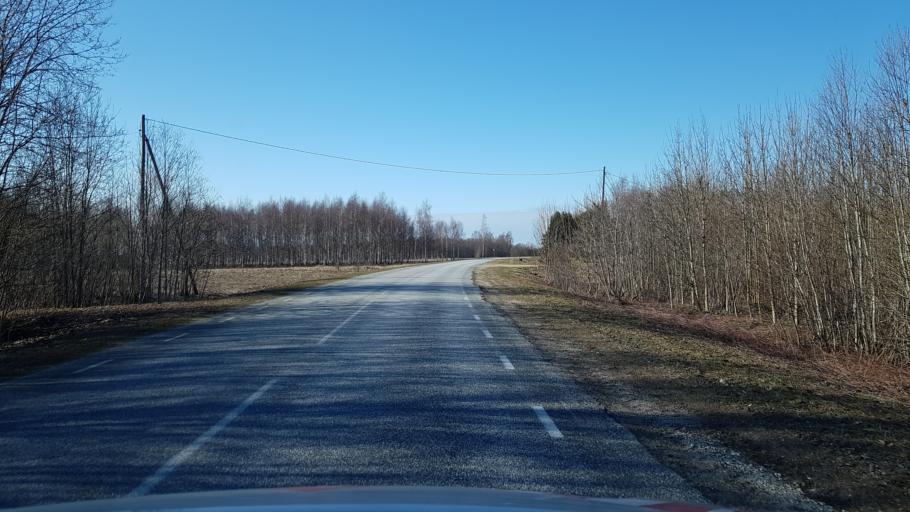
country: EE
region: Laeaene-Virumaa
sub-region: Haljala vald
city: Haljala
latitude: 59.4774
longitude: 26.1588
